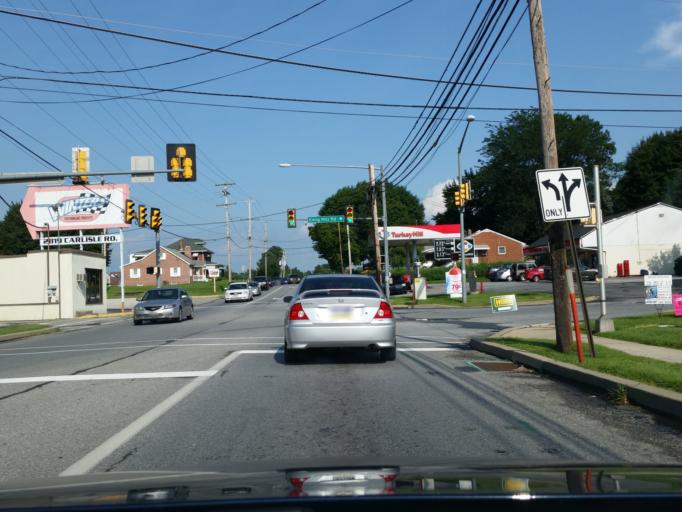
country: US
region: Pennsylvania
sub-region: York County
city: Weigelstown
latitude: 39.9818
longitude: -76.8135
